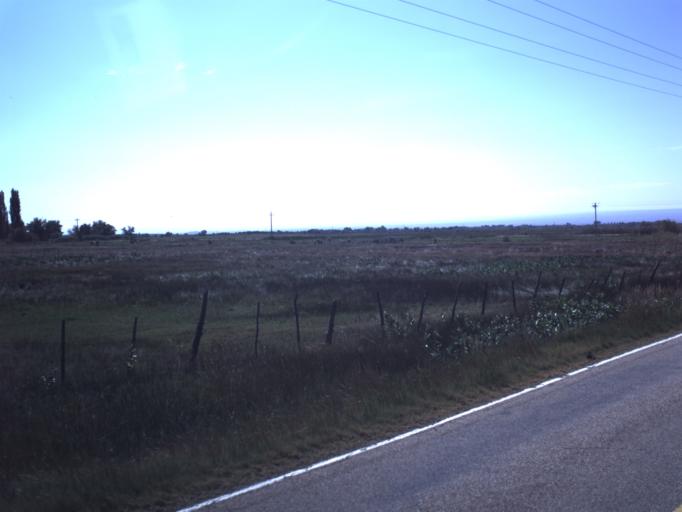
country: US
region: Utah
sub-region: Duchesne County
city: Duchesne
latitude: 40.3471
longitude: -110.2752
